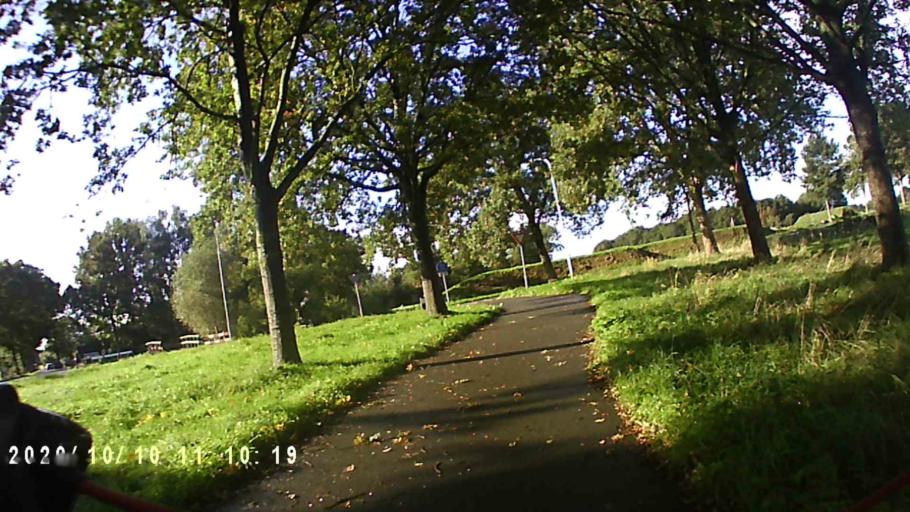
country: NL
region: Friesland
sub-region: Gemeente Smallingerland
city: Drachtstercompagnie
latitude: 53.1158
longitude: 6.2062
